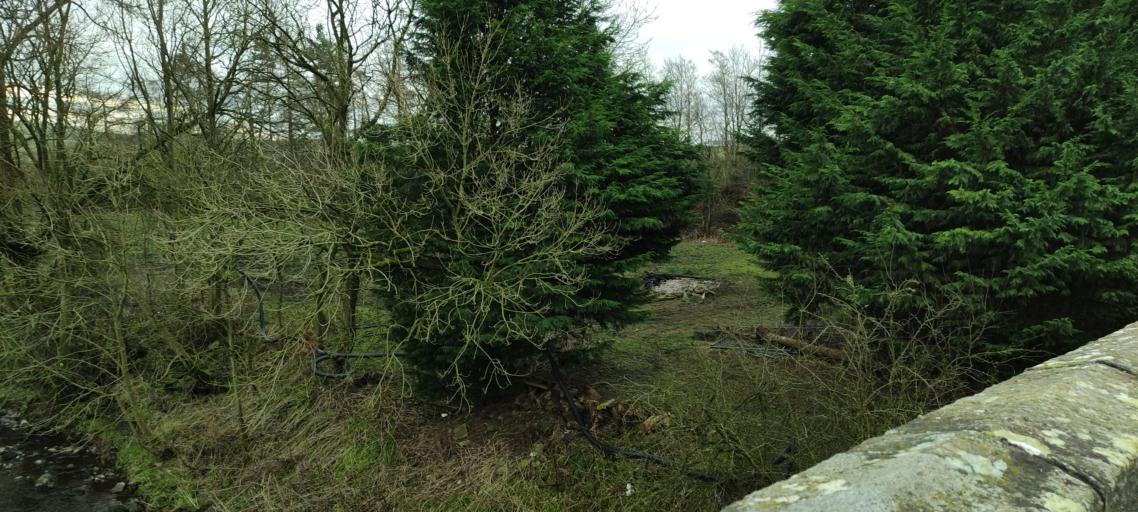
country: GB
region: England
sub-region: North Yorkshire
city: Gargrave
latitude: 53.9801
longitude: -2.1266
